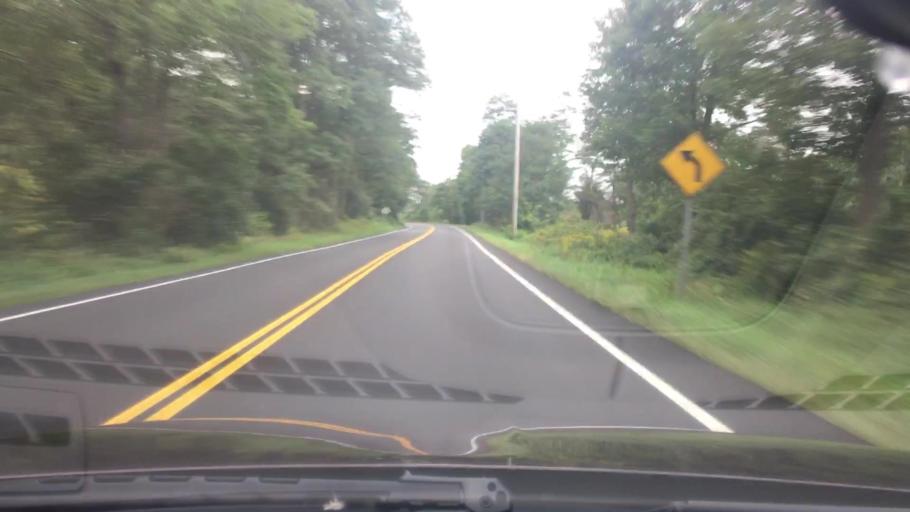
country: US
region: New York
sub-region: Dutchess County
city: Dover Plains
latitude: 41.8441
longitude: -73.5965
